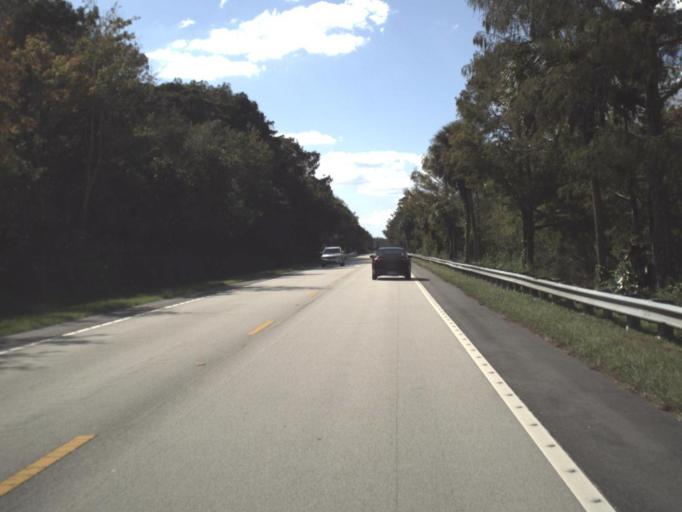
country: US
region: Florida
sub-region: Collier County
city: Marco
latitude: 25.8765
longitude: -81.2260
